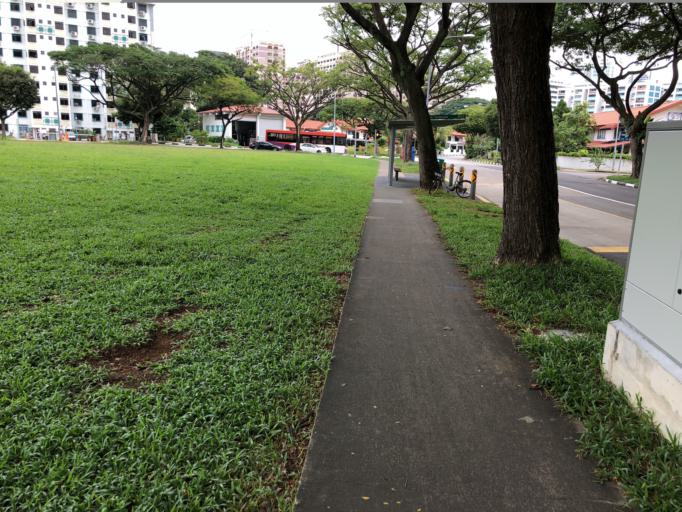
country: SG
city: Singapore
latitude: 1.3280
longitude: 103.8583
